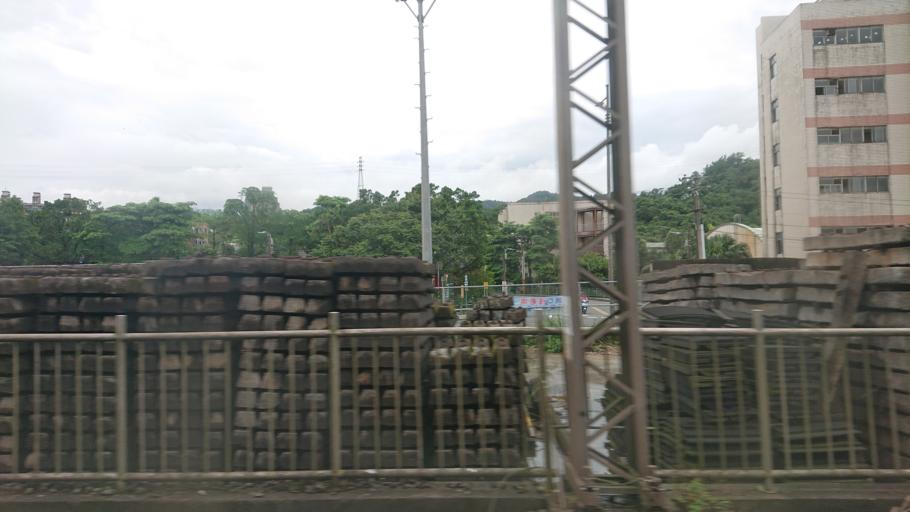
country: TW
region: Taiwan
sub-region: Keelung
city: Keelung
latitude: 25.0953
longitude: 121.7173
